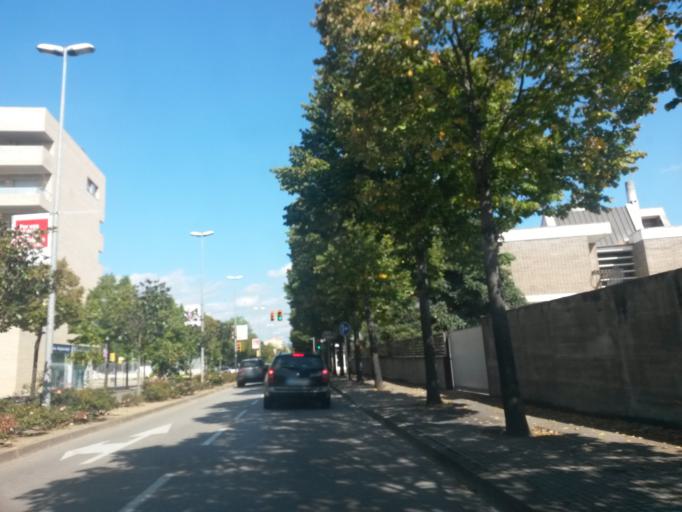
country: ES
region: Catalonia
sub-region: Provincia de Girona
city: Salt
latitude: 41.9679
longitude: 2.7874
